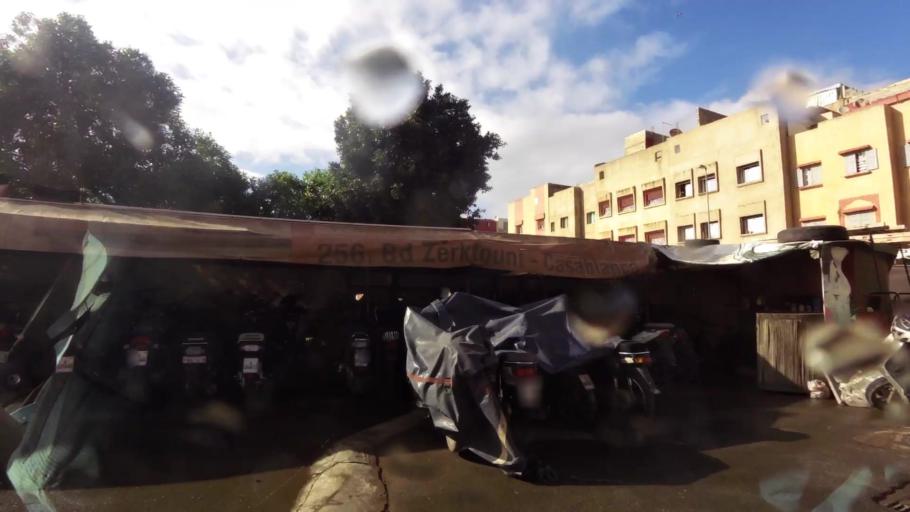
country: MA
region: Grand Casablanca
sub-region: Casablanca
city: Casablanca
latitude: 33.5572
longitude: -7.6965
